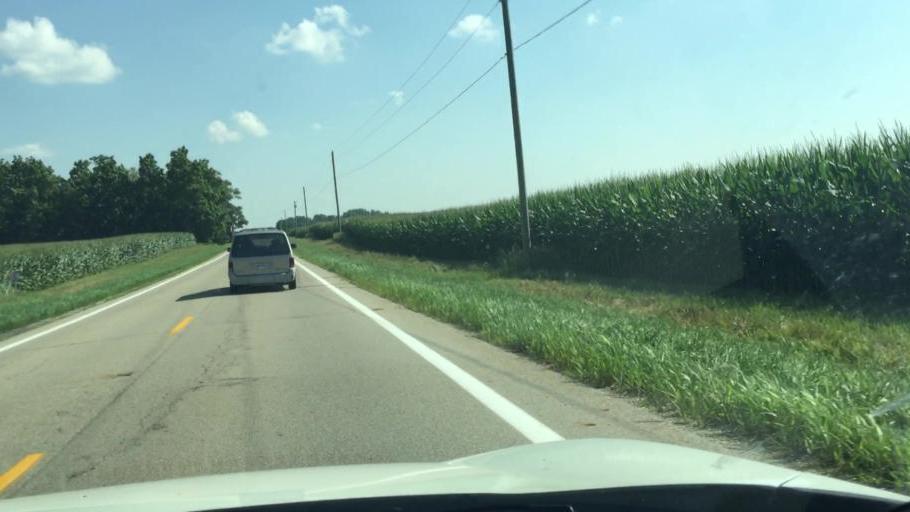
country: US
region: Ohio
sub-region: Champaign County
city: North Lewisburg
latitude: 40.1507
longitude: -83.5288
